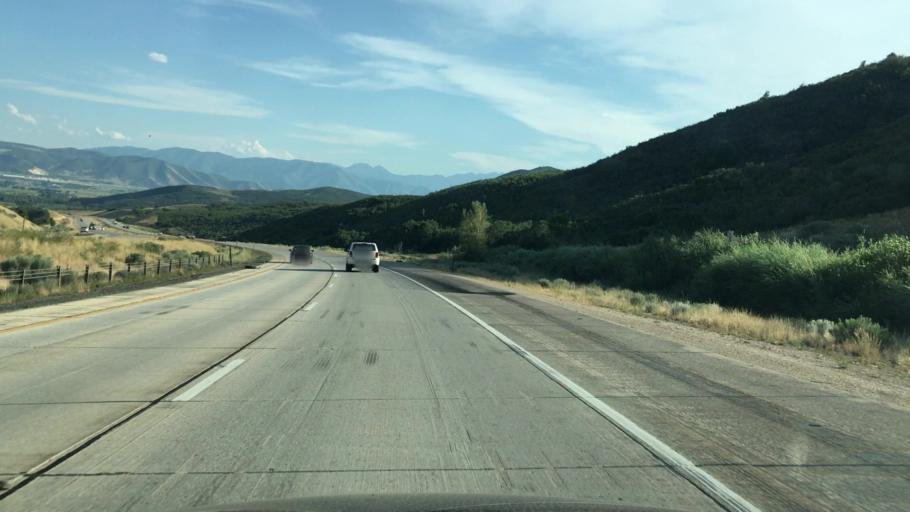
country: US
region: Utah
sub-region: Summit County
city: Park City
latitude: 40.5934
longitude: -111.4368
